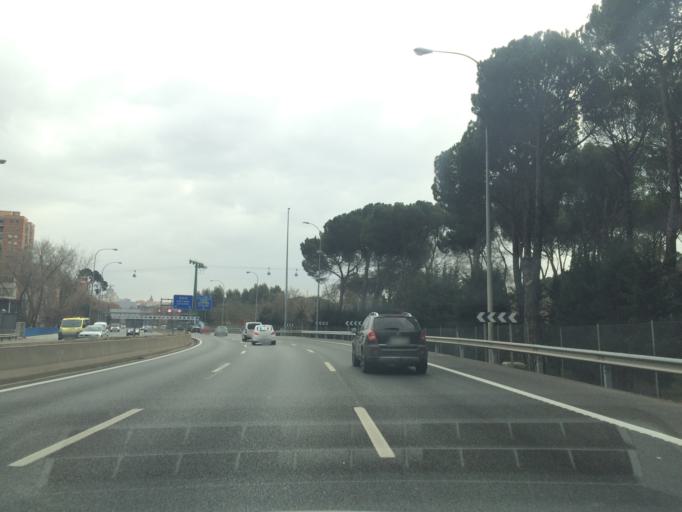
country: ES
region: Madrid
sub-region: Provincia de Madrid
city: Moncloa-Aravaca
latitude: 40.4272
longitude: -3.7347
